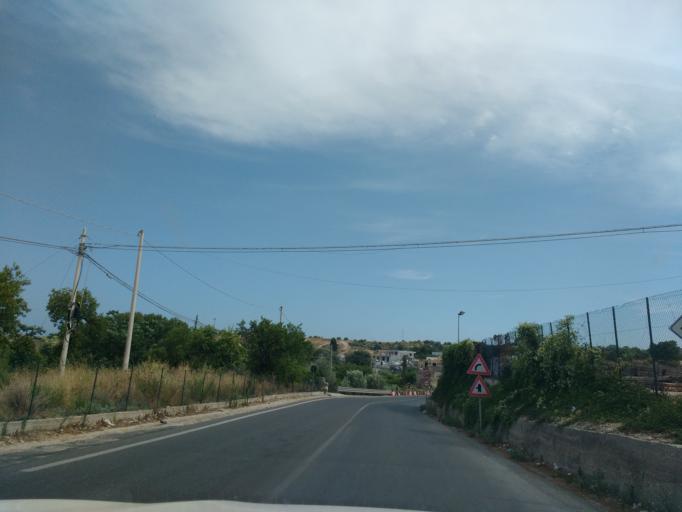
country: IT
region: Sicily
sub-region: Provincia di Siracusa
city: Noto
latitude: 36.8843
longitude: 15.0629
